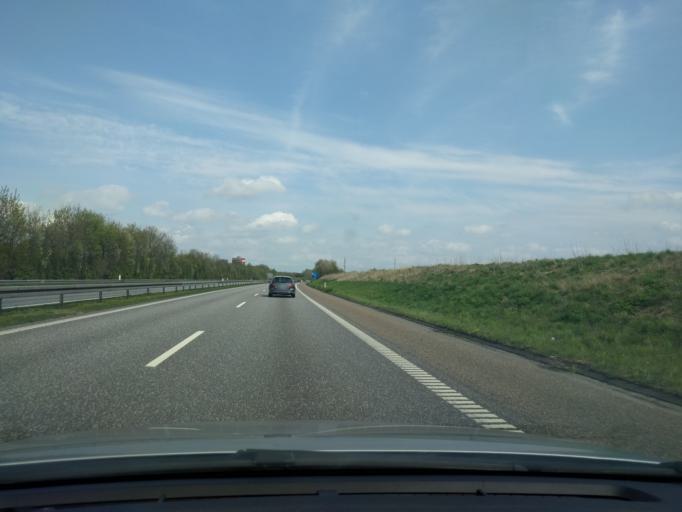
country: DK
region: Zealand
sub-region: Soro Kommune
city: Soro
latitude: 55.4540
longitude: 11.5427
